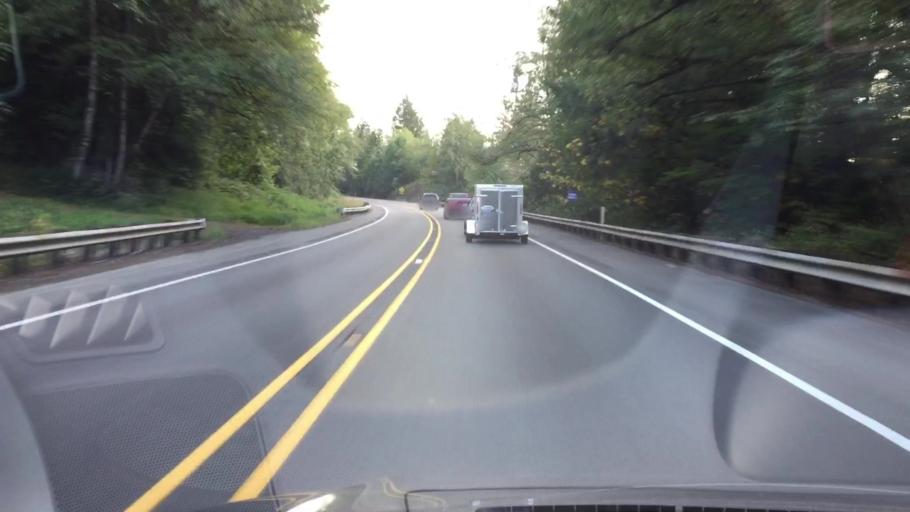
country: US
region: Washington
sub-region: Lewis County
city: Morton
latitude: 46.5324
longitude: -122.5533
